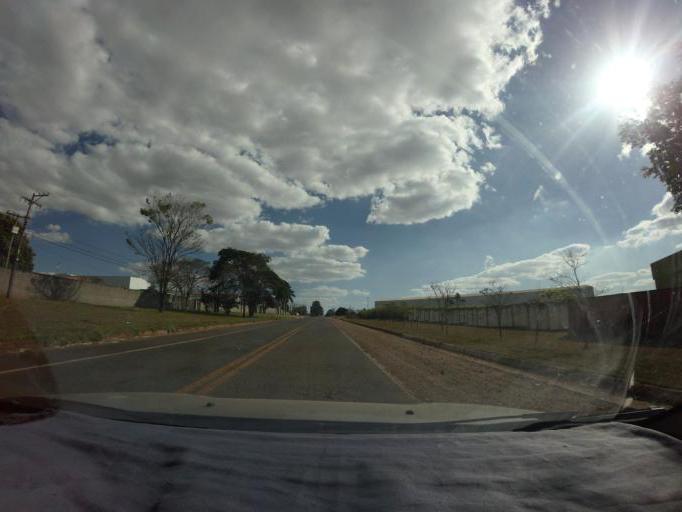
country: BR
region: Sao Paulo
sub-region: Piracicaba
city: Piracicaba
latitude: -22.7388
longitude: -47.5686
